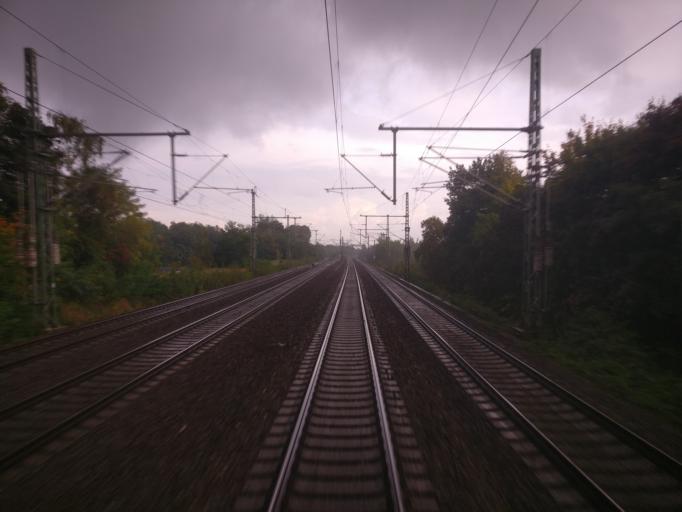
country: DE
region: Saxony
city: Dresden
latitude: 51.0235
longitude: 13.7836
